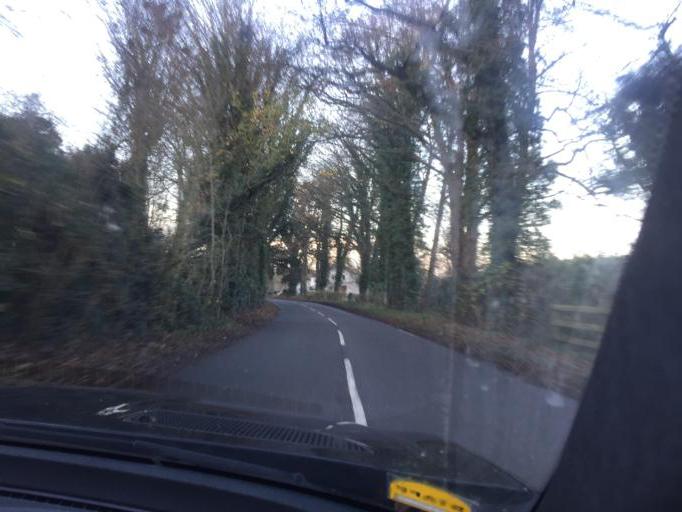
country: GB
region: England
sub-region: Northamptonshire
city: Brackley
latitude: 52.0844
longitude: -1.1456
